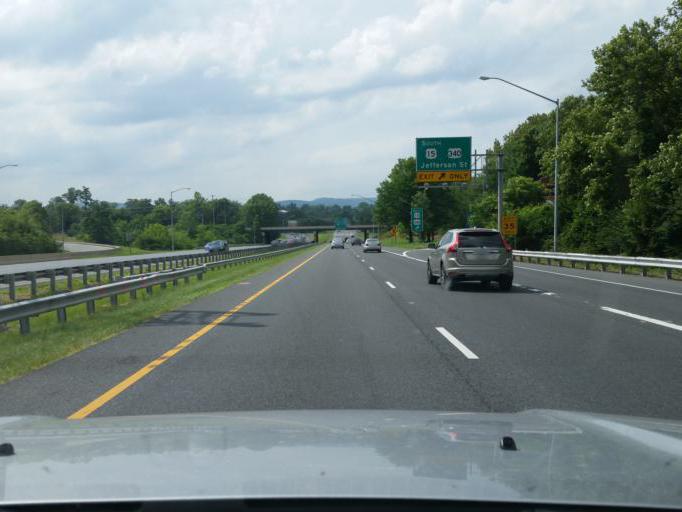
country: US
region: Maryland
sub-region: Frederick County
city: Frederick
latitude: 39.4038
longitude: -77.4304
